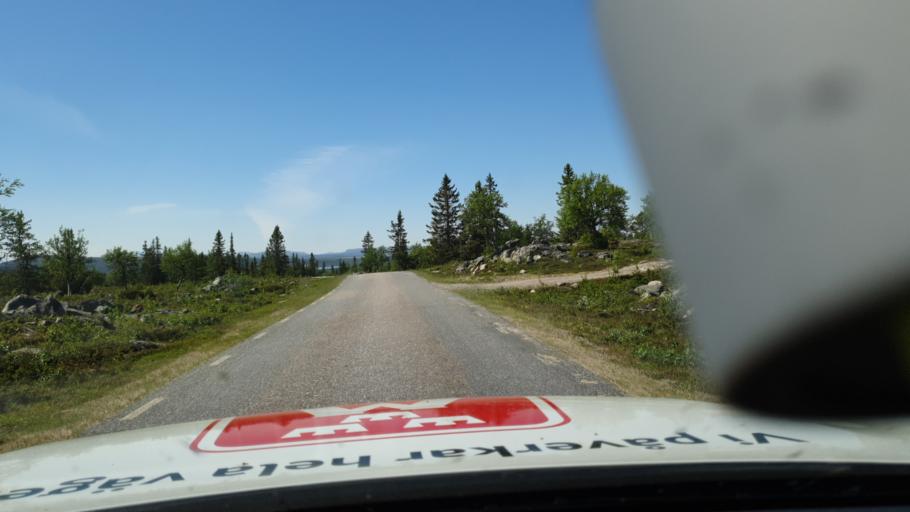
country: NO
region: Hedmark
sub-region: Trysil
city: Innbygda
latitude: 62.1365
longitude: 13.0346
